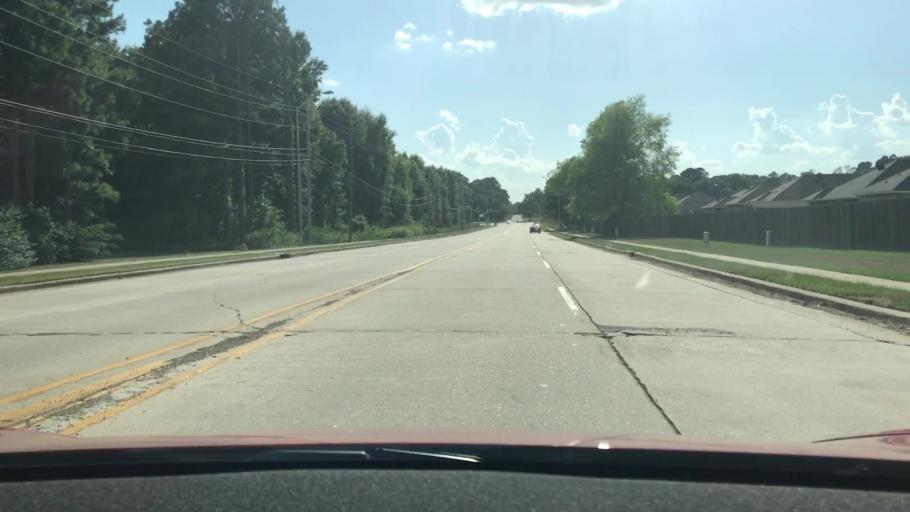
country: US
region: Louisiana
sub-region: Bossier Parish
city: Bossier City
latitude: 32.4130
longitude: -93.7752
